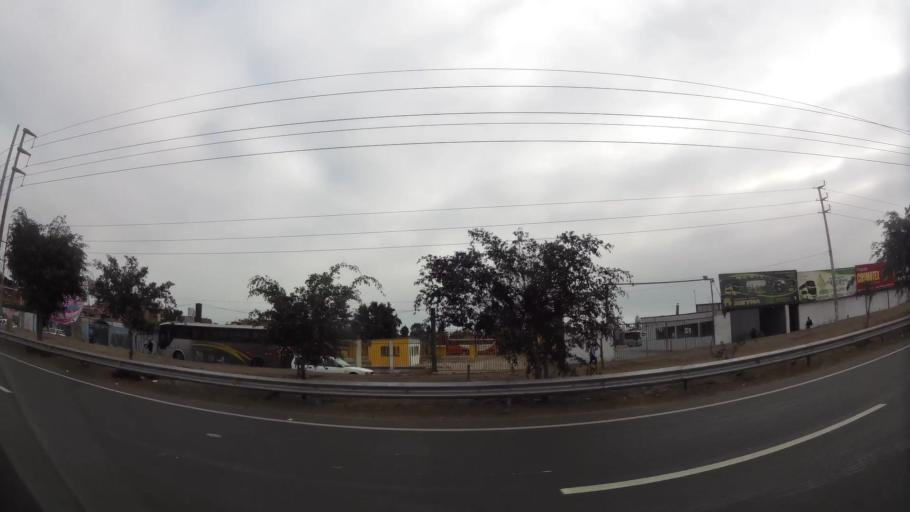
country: PE
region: Lima
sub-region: Lima
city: Surco
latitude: -12.1570
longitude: -76.9834
